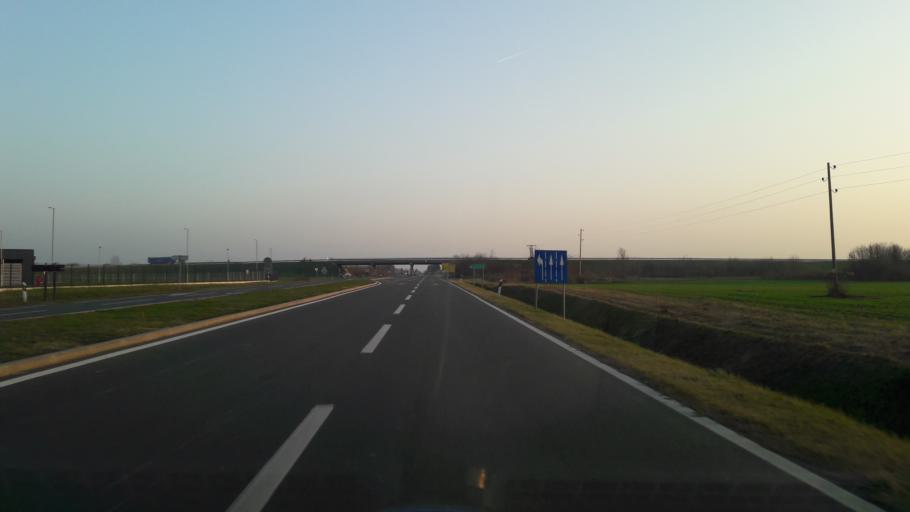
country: HR
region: Osjecko-Baranjska
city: Tenja
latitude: 45.5273
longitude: 18.7750
